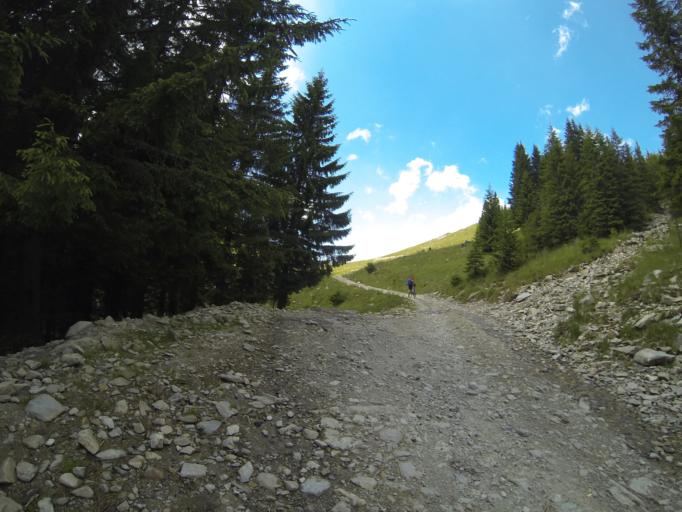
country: RO
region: Gorj
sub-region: Comuna Polovragi
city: Polovragi
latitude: 45.3463
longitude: 23.7891
